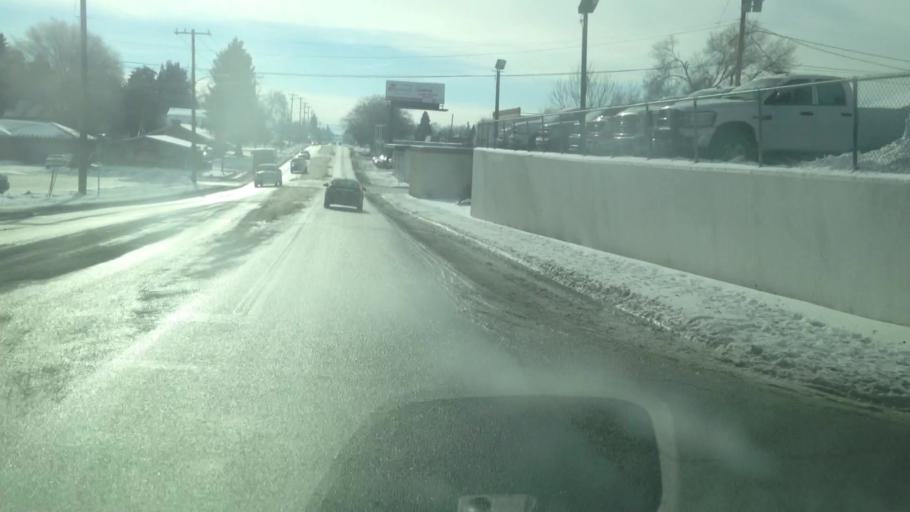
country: US
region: Idaho
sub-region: Bonneville County
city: Idaho Falls
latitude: 43.5040
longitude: -112.0239
